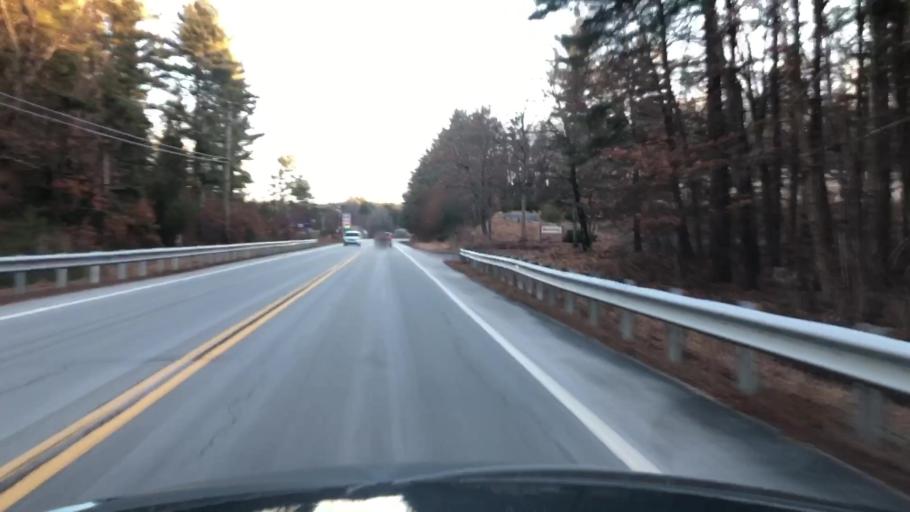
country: US
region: New Hampshire
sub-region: Hillsborough County
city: Brookline
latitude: 42.7257
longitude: -71.6630
